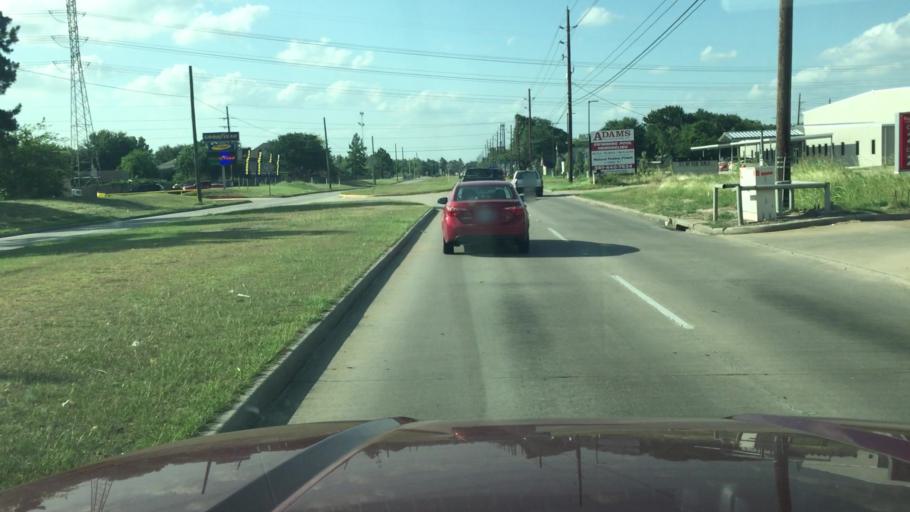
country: US
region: Texas
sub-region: Harris County
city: Hudson
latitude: 29.9529
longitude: -95.4983
